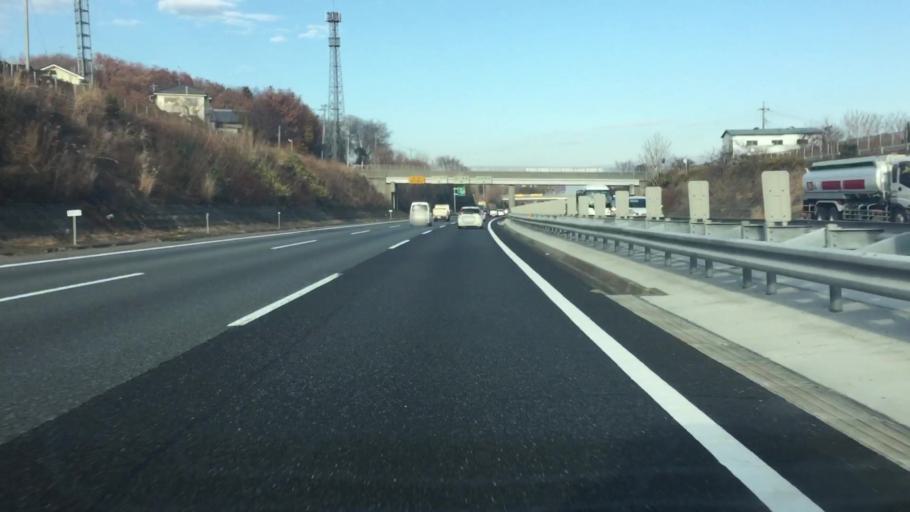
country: JP
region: Saitama
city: Yorii
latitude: 36.1658
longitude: 139.2008
